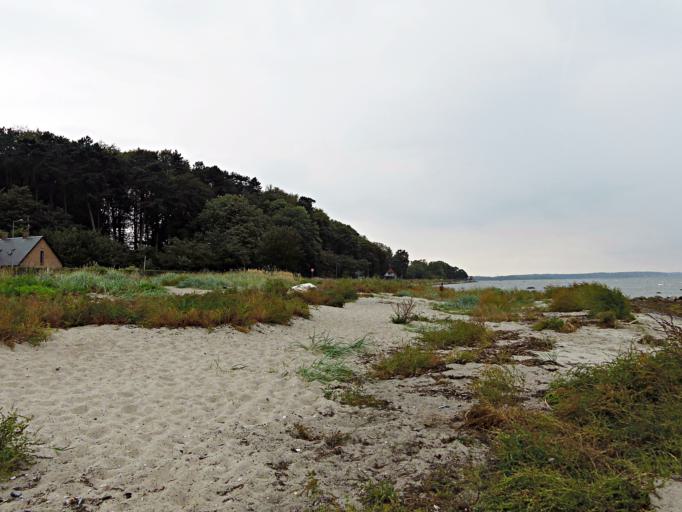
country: DK
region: Capital Region
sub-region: Fredensborg Kommune
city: Kokkedal
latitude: 55.9052
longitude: 12.5290
